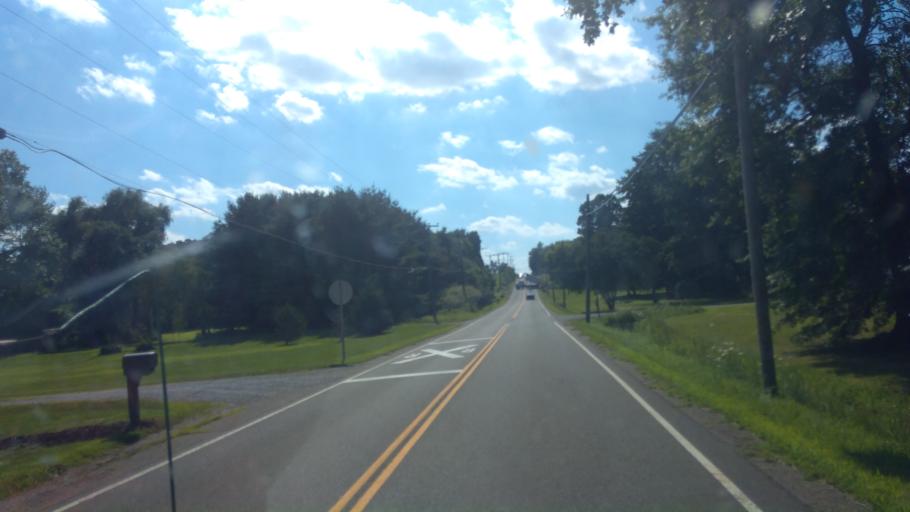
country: US
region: Ohio
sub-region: Stark County
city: Navarre
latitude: 40.7267
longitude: -81.5621
